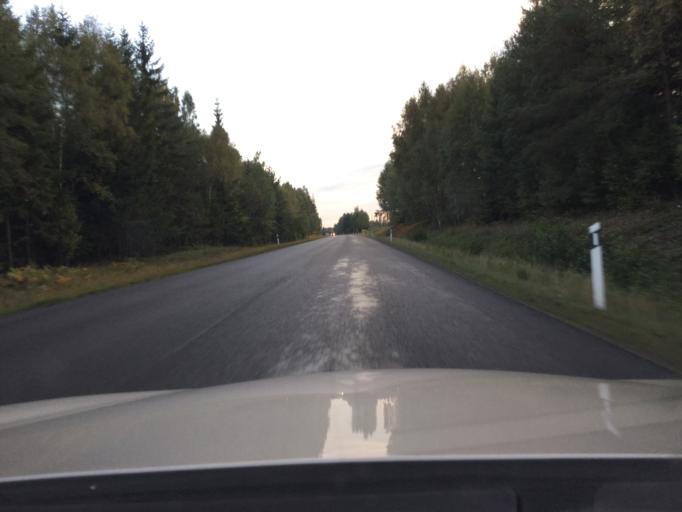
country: SE
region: Kronoberg
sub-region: Almhults Kommun
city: AElmhult
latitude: 56.6027
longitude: 14.2187
